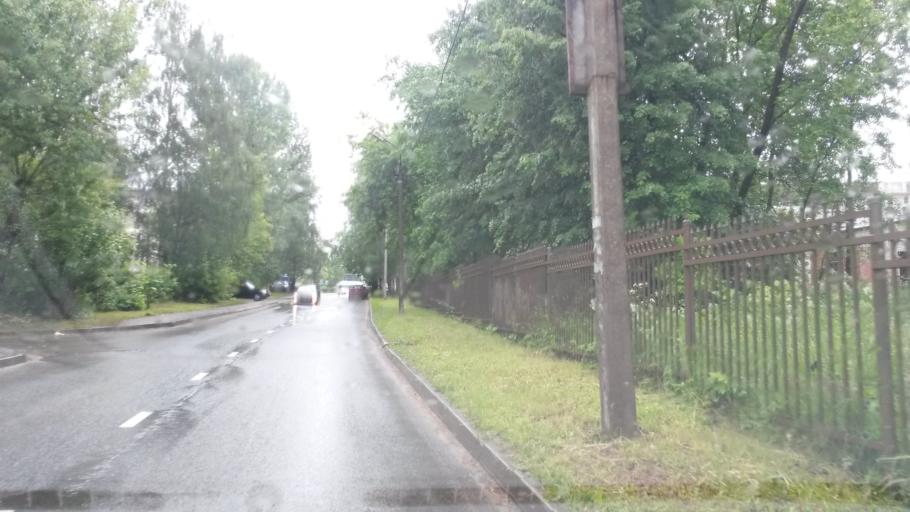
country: RU
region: Jaroslavl
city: Yaroslavl
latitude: 57.5895
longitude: 39.8423
